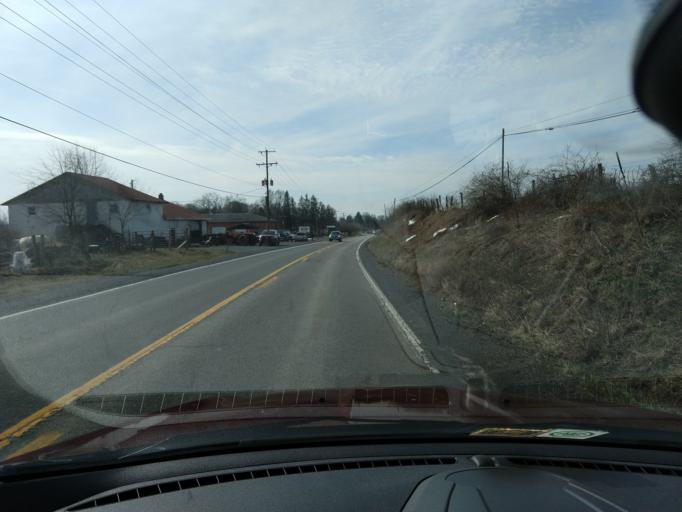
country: US
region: West Virginia
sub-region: Greenbrier County
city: Lewisburg
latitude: 37.8615
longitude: -80.4105
